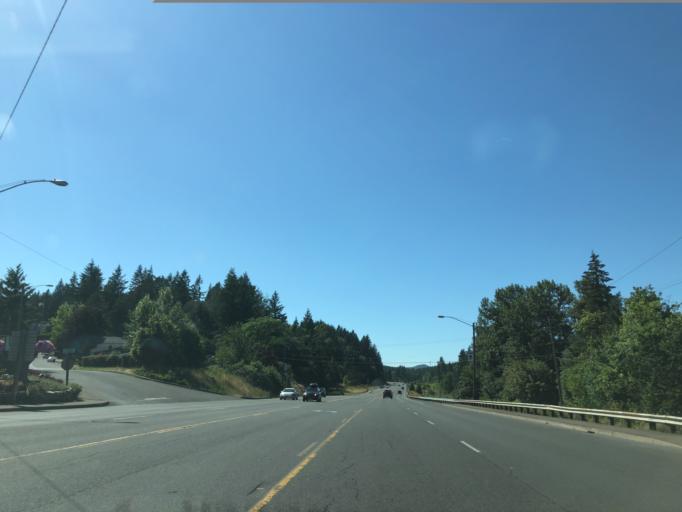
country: US
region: Oregon
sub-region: Linn County
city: Sweet Home
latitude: 44.4000
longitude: -122.7420
